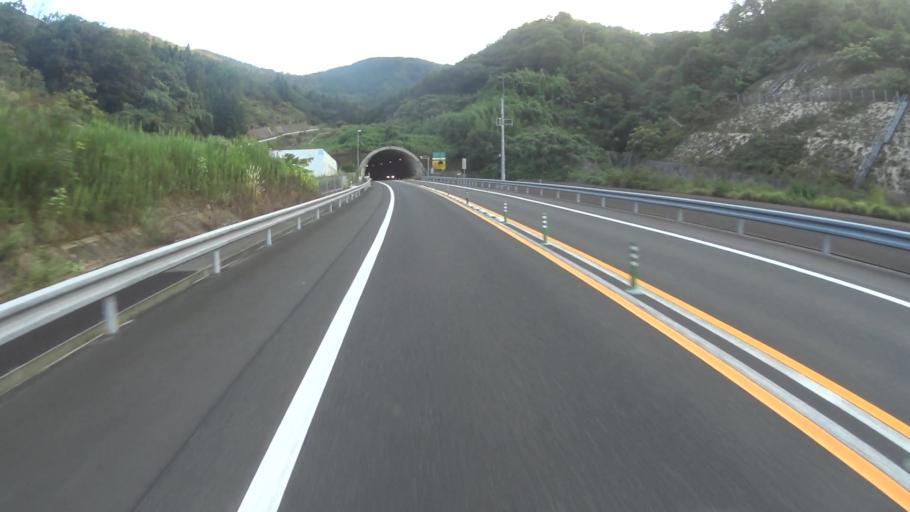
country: JP
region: Kyoto
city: Miyazu
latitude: 35.4930
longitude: 135.1724
